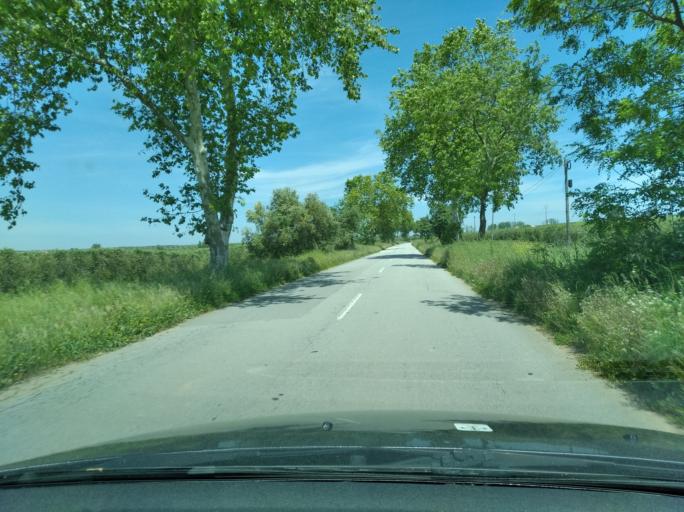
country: PT
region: Portalegre
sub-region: Avis
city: Avis
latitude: 39.0765
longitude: -7.8811
